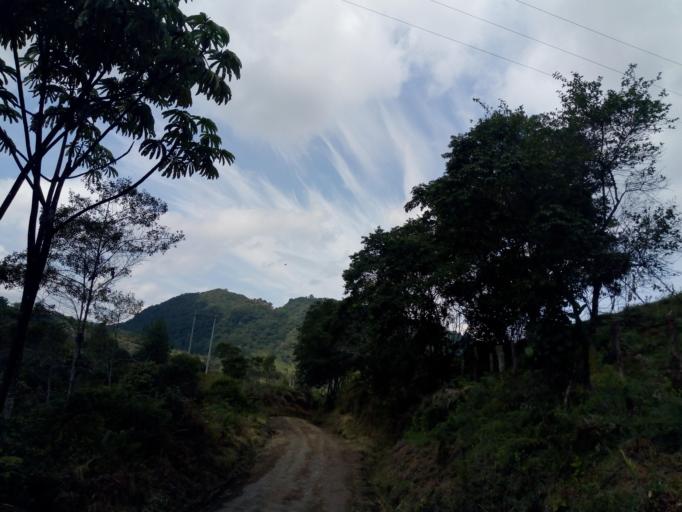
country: CO
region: Boyaca
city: Moniquira
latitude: 5.8653
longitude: -73.5215
